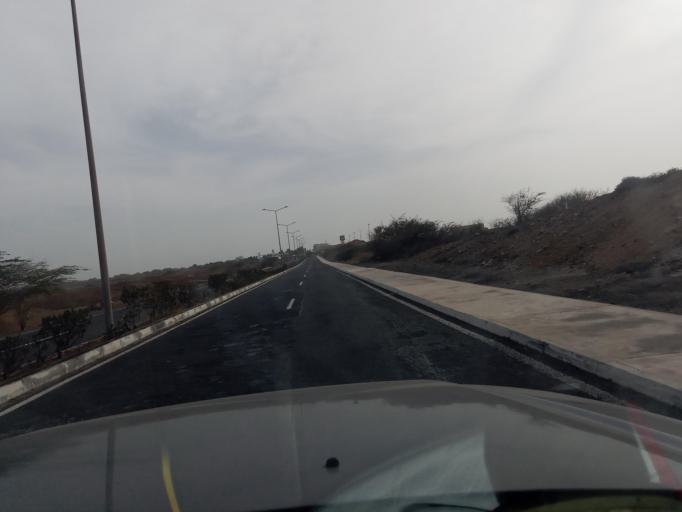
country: CV
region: Sal
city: Espargos
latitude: 16.7419
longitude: -22.9437
